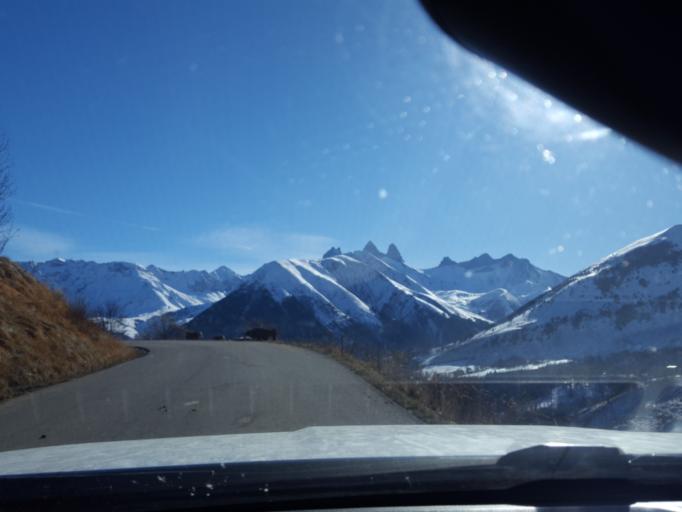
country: FR
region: Rhone-Alpes
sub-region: Departement de la Savoie
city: Saint-Jean-de-Maurienne
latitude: 45.2129
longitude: 6.2602
